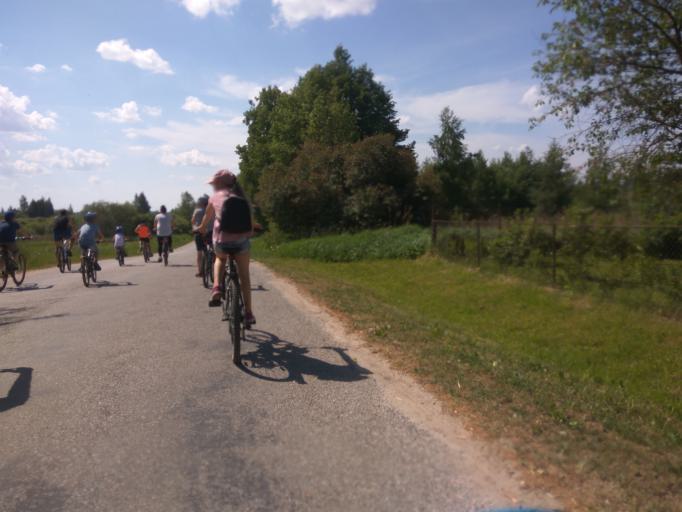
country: LV
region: Kuldigas Rajons
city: Kuldiga
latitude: 56.9564
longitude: 21.9731
